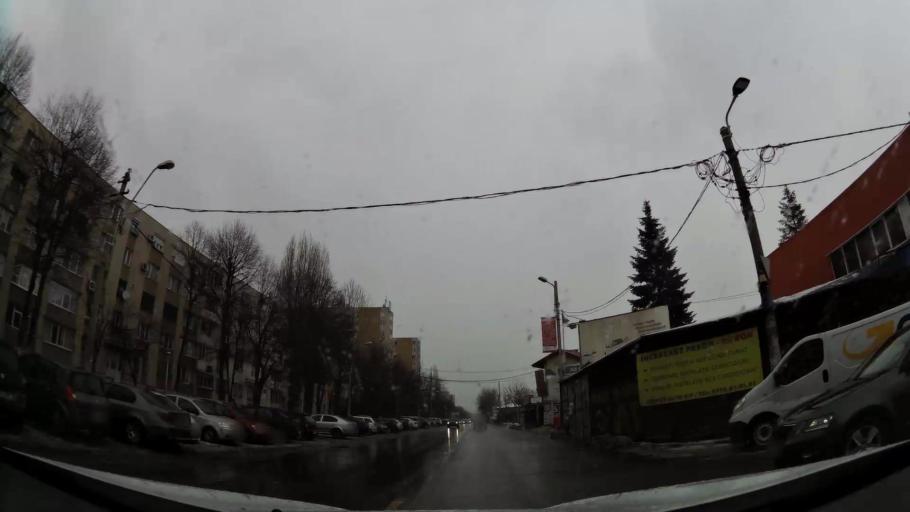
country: RO
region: Ilfov
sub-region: Comuna Chiajna
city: Rosu
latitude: 44.4132
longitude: 26.0269
